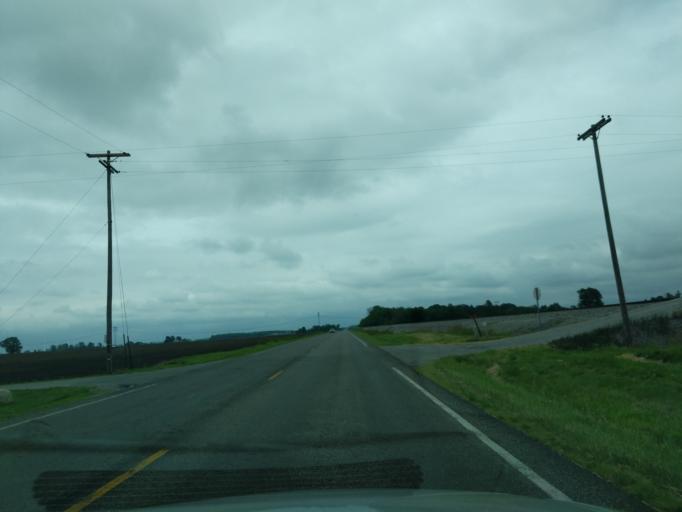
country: US
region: Indiana
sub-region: Madison County
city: Elwood
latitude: 40.2806
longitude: -85.9193
